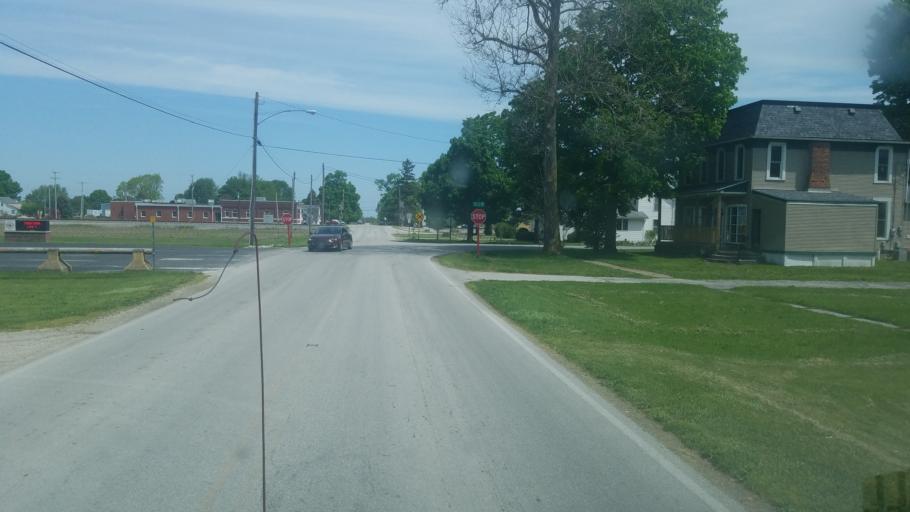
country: US
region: Ohio
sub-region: Sandusky County
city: Ballville
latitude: 41.2388
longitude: -83.1496
